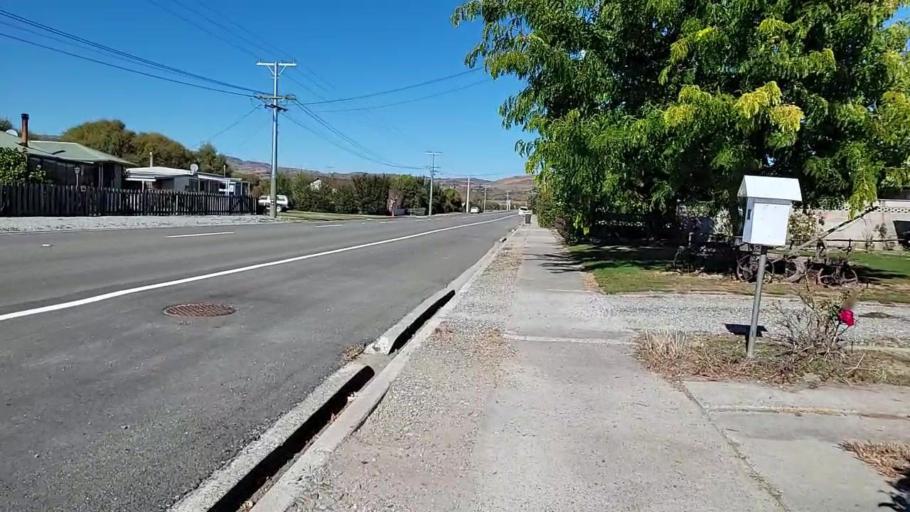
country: NZ
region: Otago
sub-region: Queenstown-Lakes District
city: Wanaka
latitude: -45.1025
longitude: 169.5957
